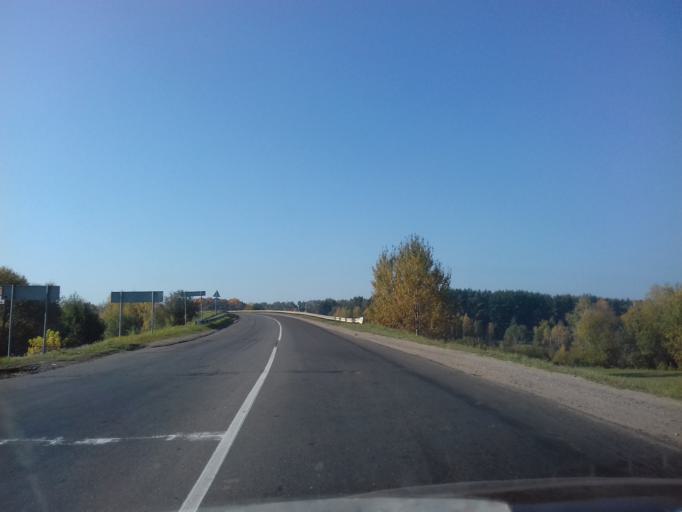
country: BY
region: Minsk
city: Hatava
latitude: 53.7767
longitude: 27.6432
